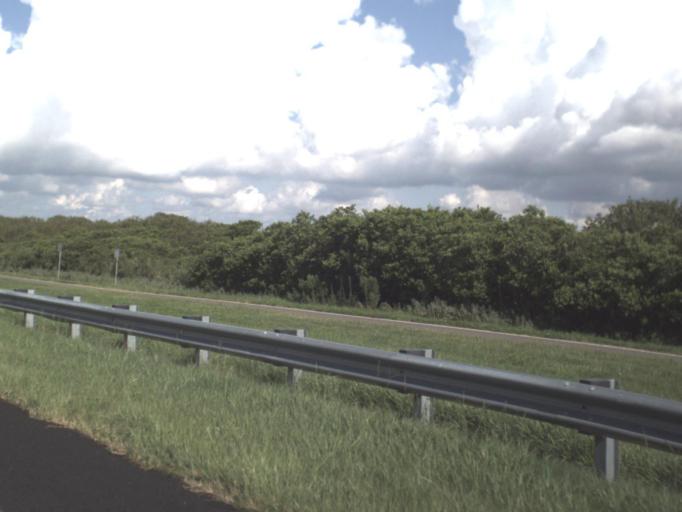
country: US
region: Florida
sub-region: Hillsborough County
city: Town 'n' Country
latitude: 27.9733
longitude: -82.5959
